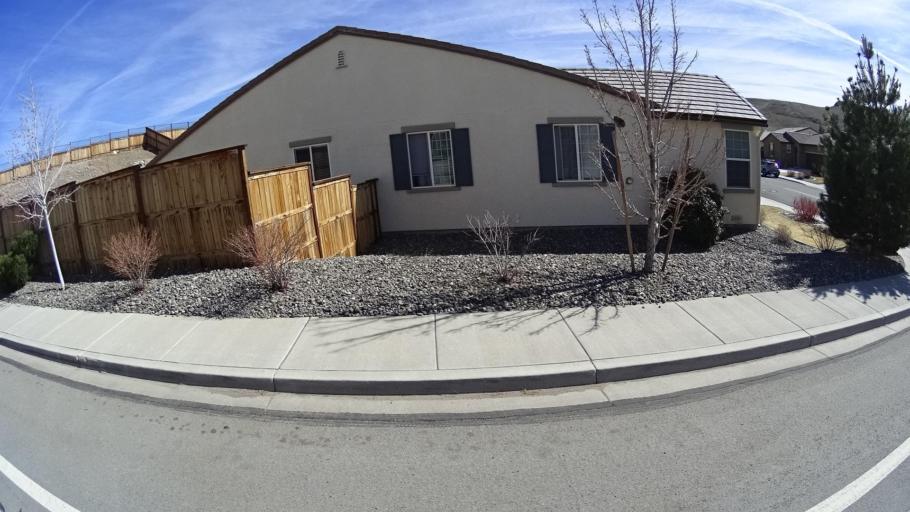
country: US
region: Nevada
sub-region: Washoe County
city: Spanish Springs
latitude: 39.5821
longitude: -119.6889
